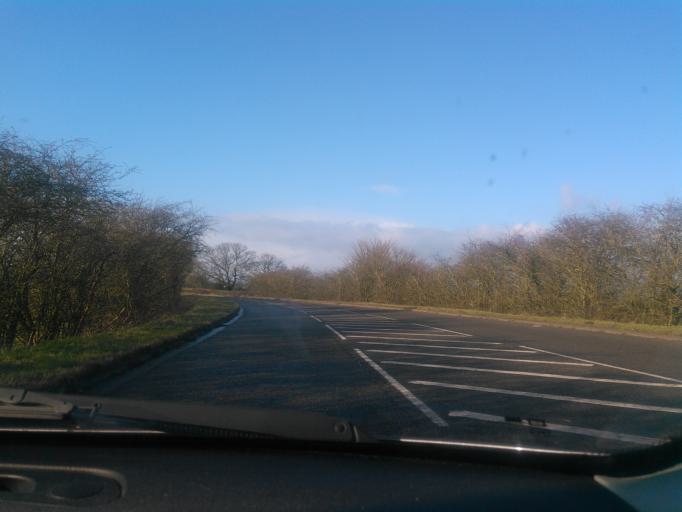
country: GB
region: England
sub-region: Telford and Wrekin
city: Eyton upon the Weald Moors
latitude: 52.7315
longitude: -2.5497
